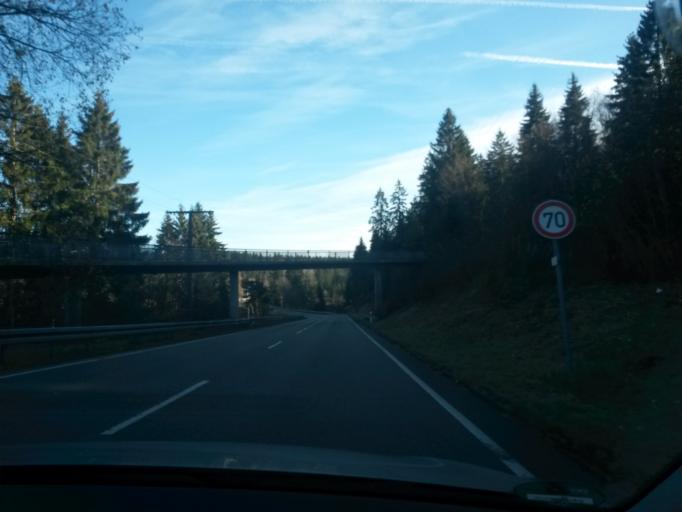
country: DE
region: Baden-Wuerttemberg
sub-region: Karlsruhe Region
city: Baiersbronn
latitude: 48.4711
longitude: 8.3103
